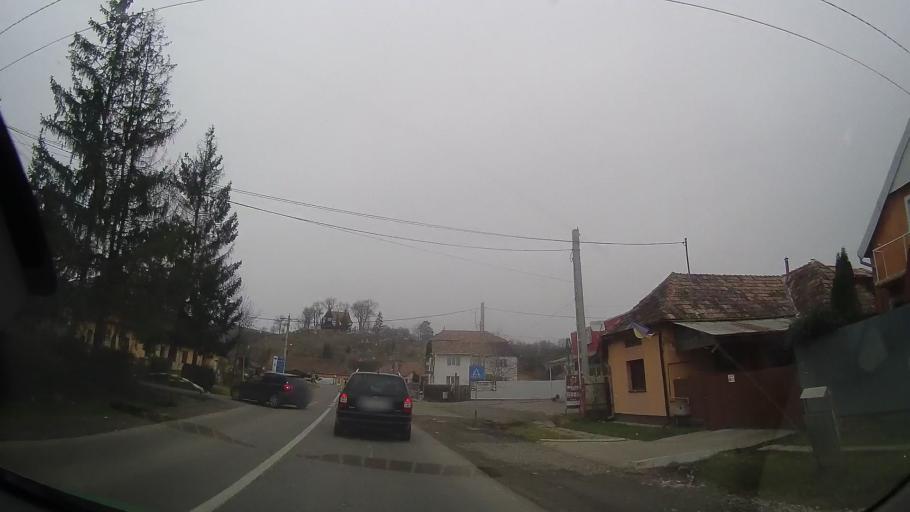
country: RO
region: Mures
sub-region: Comuna Ceausu de Campie
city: Ceausu de Campie
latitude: 46.6401
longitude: 24.5166
